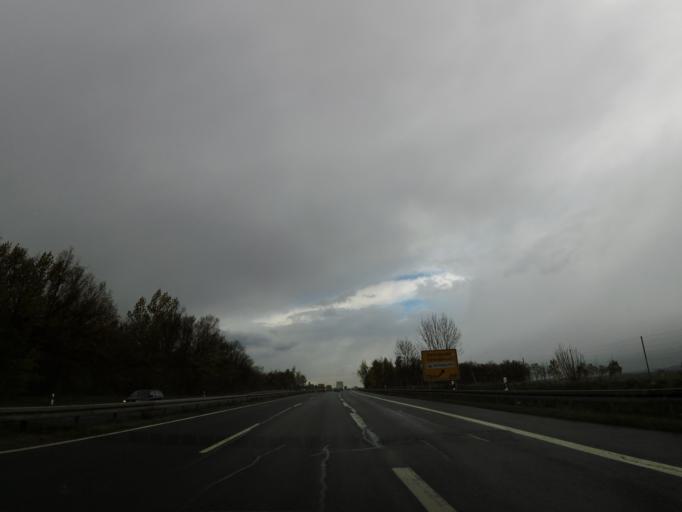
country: DE
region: Lower Saxony
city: Bad Harzburg
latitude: 51.9140
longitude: 10.5540
